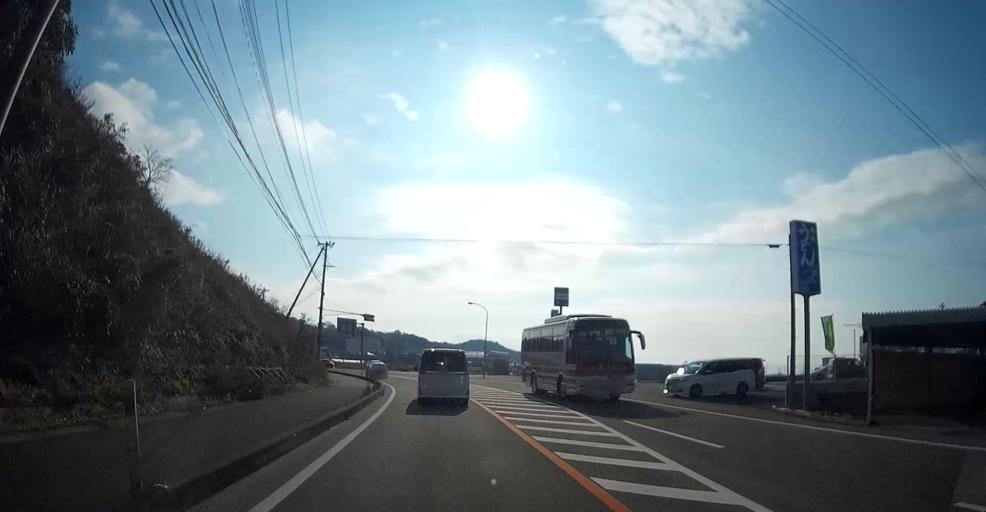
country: JP
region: Kumamoto
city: Yatsushiro
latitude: 32.5755
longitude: 130.4200
